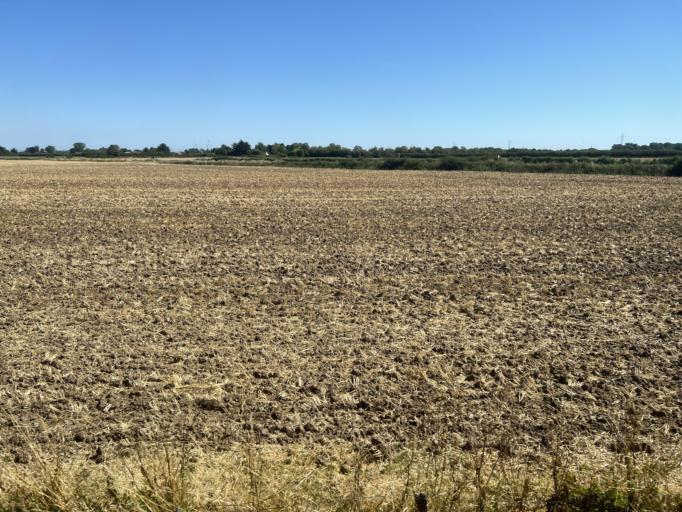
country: GB
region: England
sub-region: Lincolnshire
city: Wainfleet All Saints
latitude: 53.1245
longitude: 0.1981
